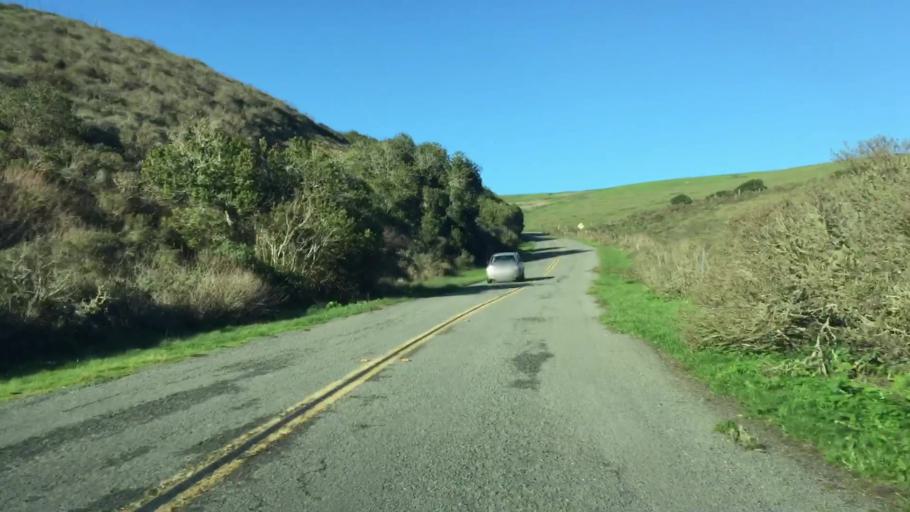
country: US
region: California
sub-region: Marin County
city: Inverness
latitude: 38.1672
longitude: -122.9374
